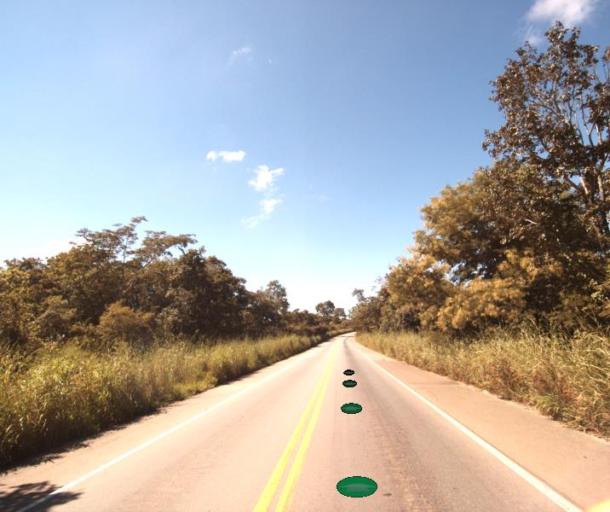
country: BR
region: Goias
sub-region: Jaragua
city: Jaragua
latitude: -15.5817
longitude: -49.4143
